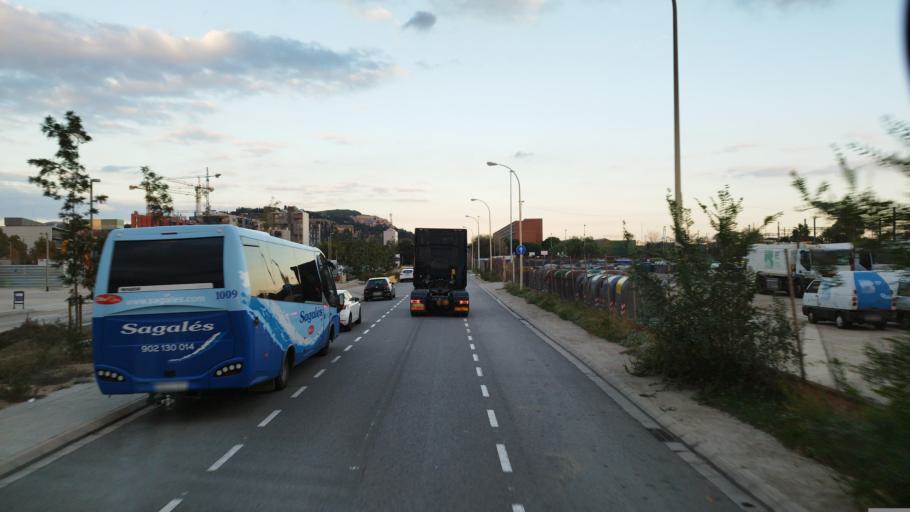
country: ES
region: Catalonia
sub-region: Provincia de Barcelona
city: Sants-Montjuic
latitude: 41.3487
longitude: 2.1390
